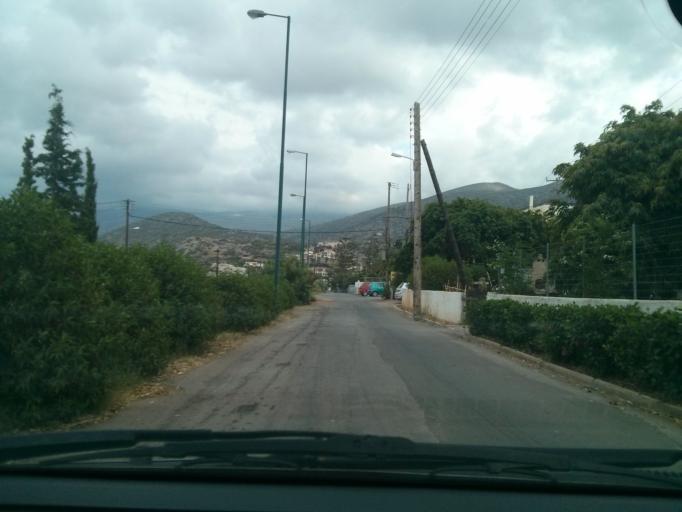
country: GR
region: Crete
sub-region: Nomos Irakleiou
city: Stalis
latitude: 35.2964
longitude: 25.4219
